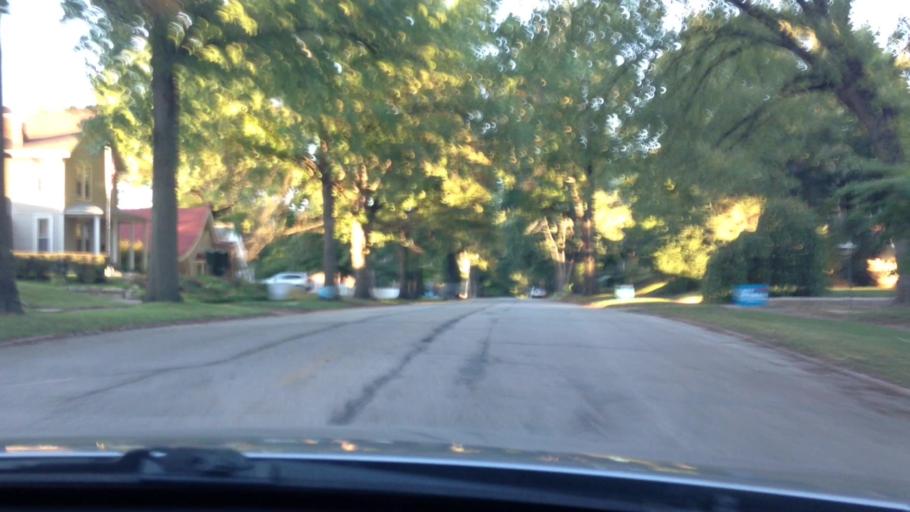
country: US
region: Kansas
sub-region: Leavenworth County
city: Leavenworth
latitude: 39.3035
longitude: -94.9208
